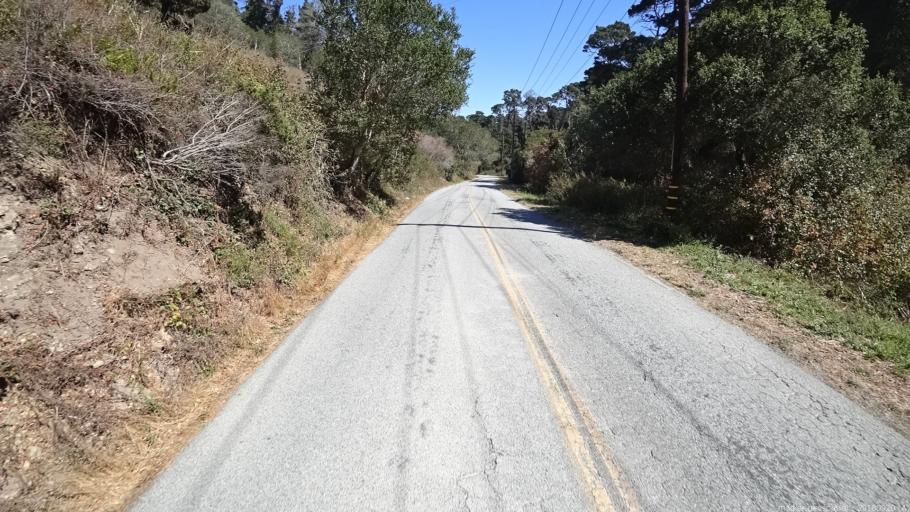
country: US
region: California
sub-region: Monterey County
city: Monterey
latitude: 36.5733
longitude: -121.8768
